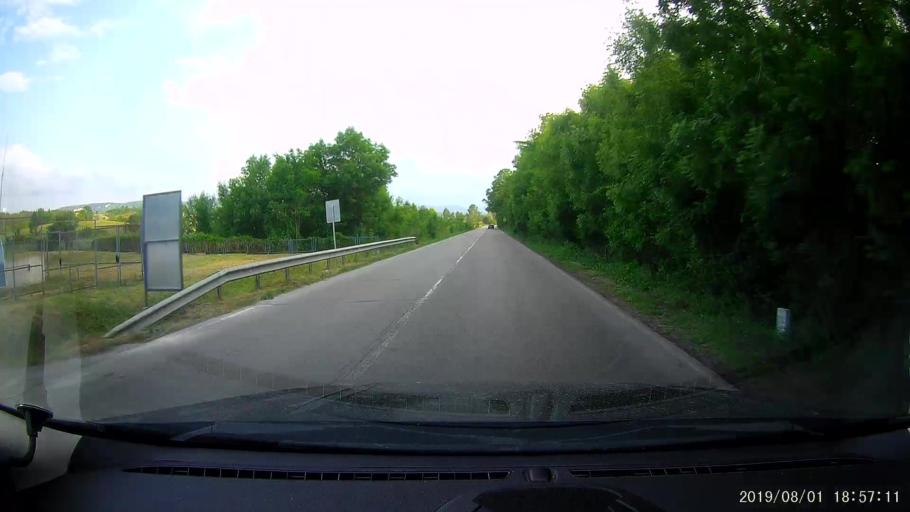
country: BG
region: Shumen
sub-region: Obshtina Smyadovo
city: Smyadovo
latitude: 43.1515
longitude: 27.0214
